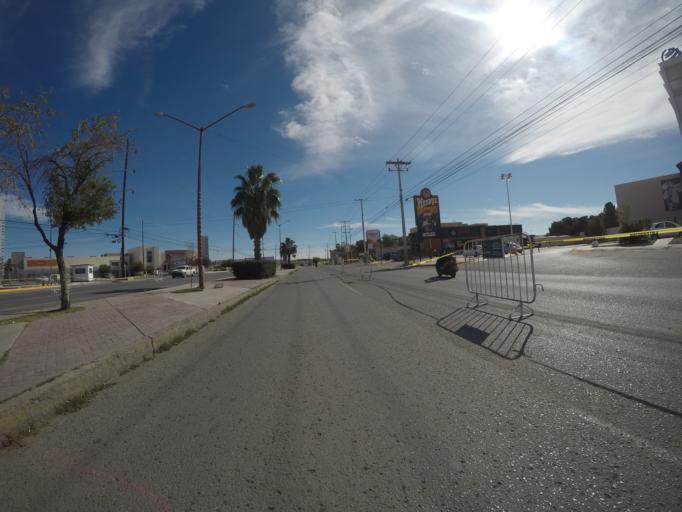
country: MX
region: Chihuahua
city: Ciudad Juarez
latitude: 31.7248
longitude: -106.4022
